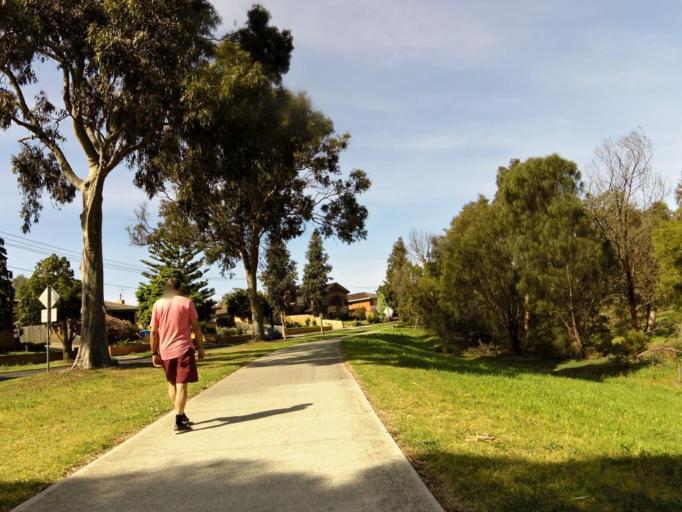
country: AU
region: Victoria
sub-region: Brimbank
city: Deer Park
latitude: -37.7654
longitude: 144.7685
